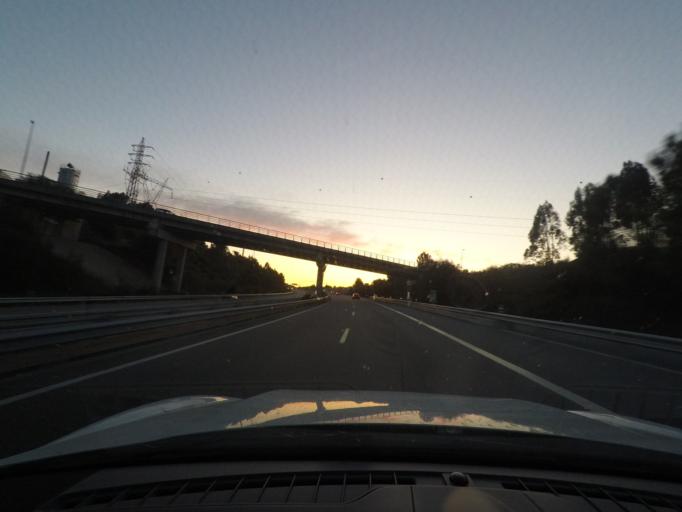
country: PT
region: Porto
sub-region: Pacos de Ferreira
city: Seroa
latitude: 41.2554
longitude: -8.4173
